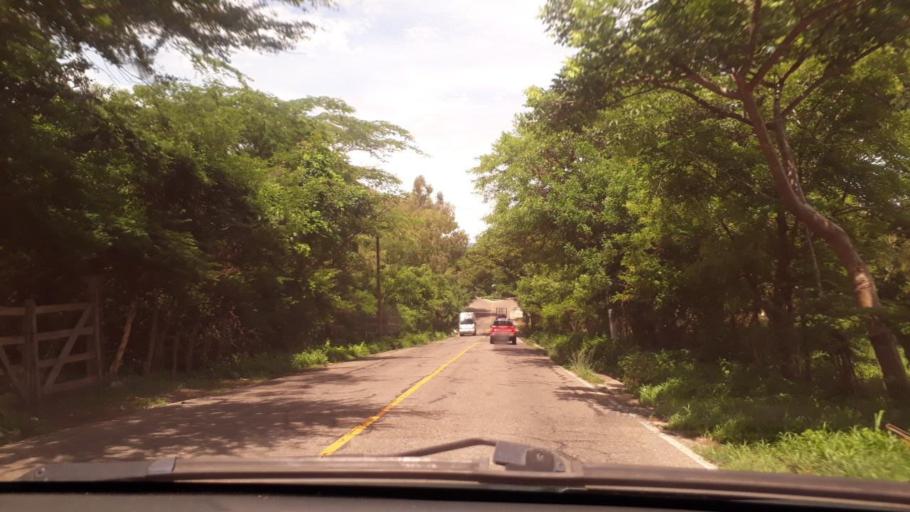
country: GT
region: Jutiapa
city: Jalpatagua
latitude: 14.1605
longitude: -90.0527
